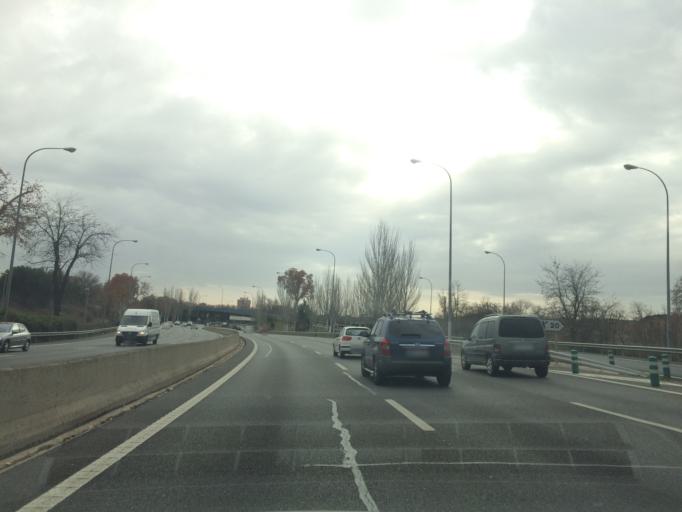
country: ES
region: Madrid
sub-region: Provincia de Madrid
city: Moncloa-Aravaca
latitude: 40.4407
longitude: -3.7389
